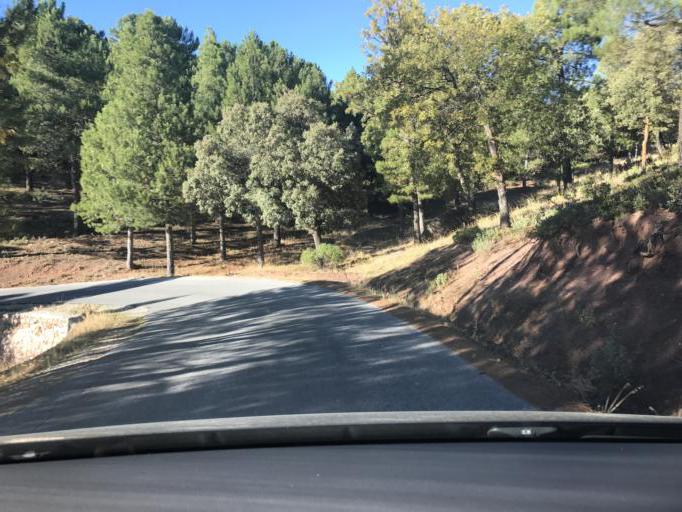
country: ES
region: Andalusia
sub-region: Provincia de Granada
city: Beas de Granada
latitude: 37.3065
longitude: -3.4542
